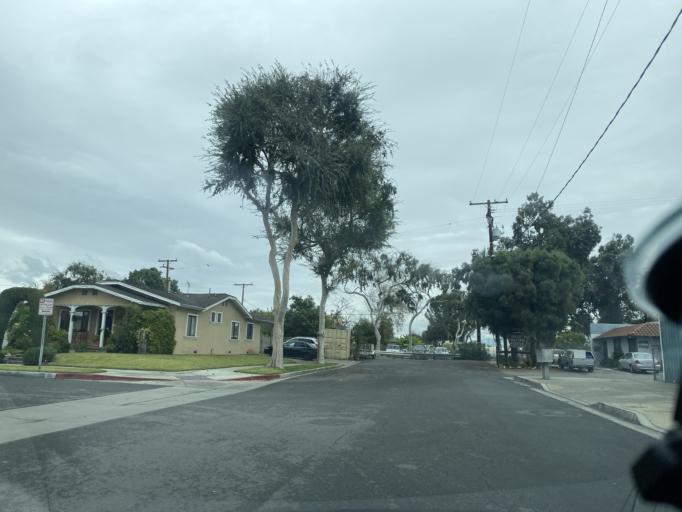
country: US
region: California
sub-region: Orange County
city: Fullerton
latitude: 33.8684
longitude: -117.9098
